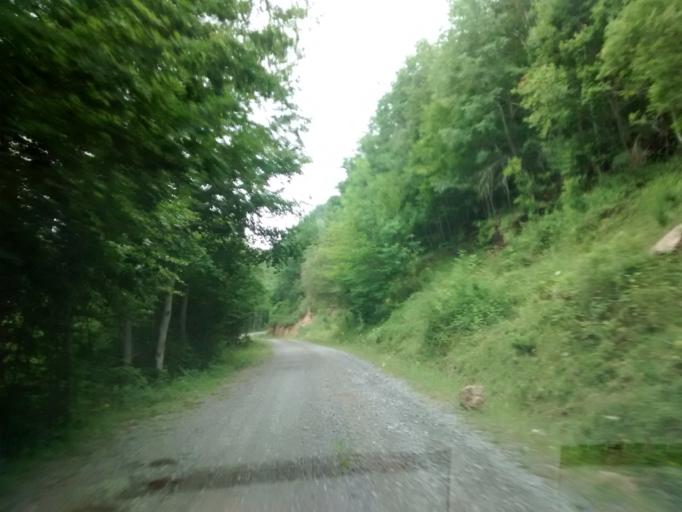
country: ES
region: La Rioja
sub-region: Provincia de La Rioja
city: Ajamil
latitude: 42.1515
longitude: -2.4807
